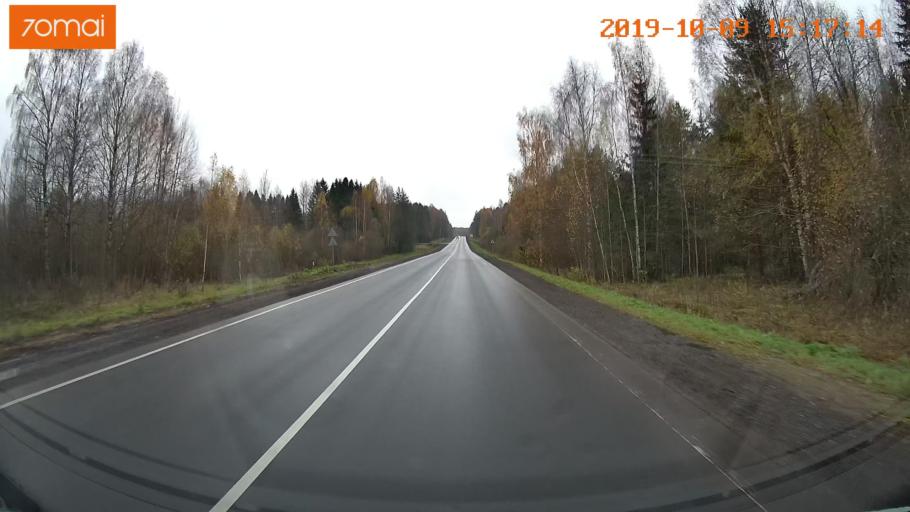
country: RU
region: Kostroma
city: Susanino
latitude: 58.1010
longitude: 41.5835
